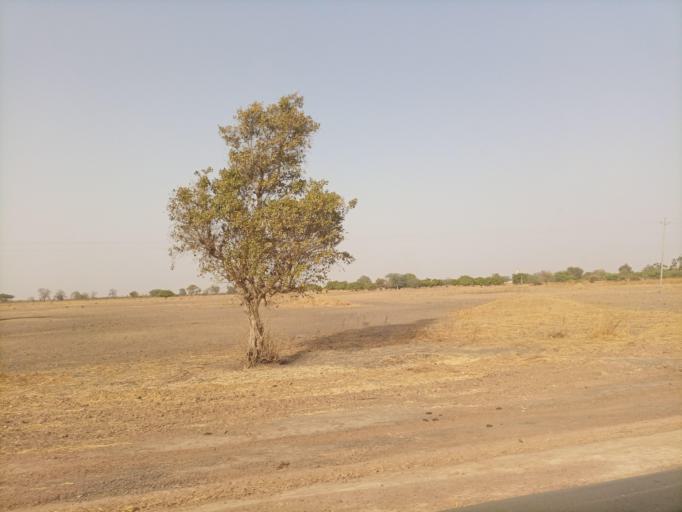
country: SN
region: Fatick
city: Passi
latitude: 14.0251
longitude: -16.3026
